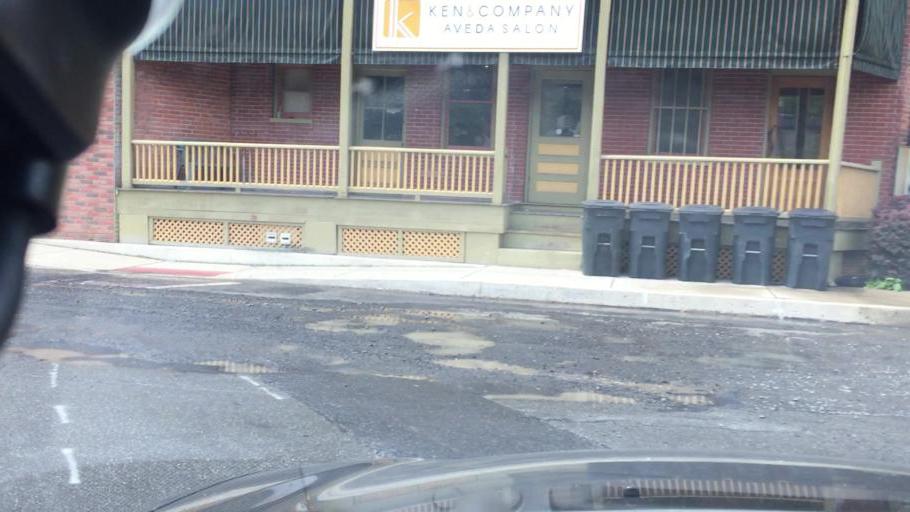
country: US
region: Pennsylvania
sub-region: Monroe County
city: Stroudsburg
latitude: 40.9859
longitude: -75.1906
